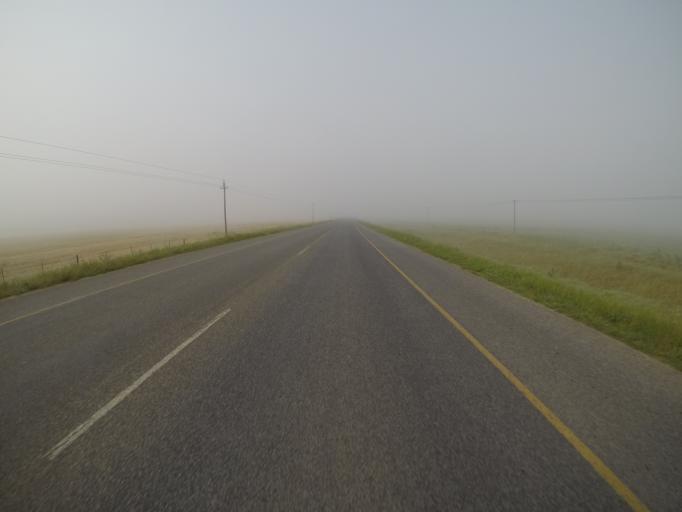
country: ZA
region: Western Cape
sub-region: City of Cape Town
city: Kraaifontein
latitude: -33.6749
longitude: 18.7068
